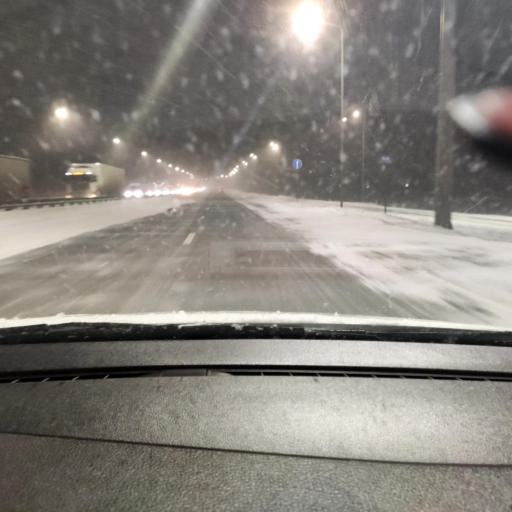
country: RU
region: Tatarstan
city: Pestretsy
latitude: 55.6735
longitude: 49.7064
